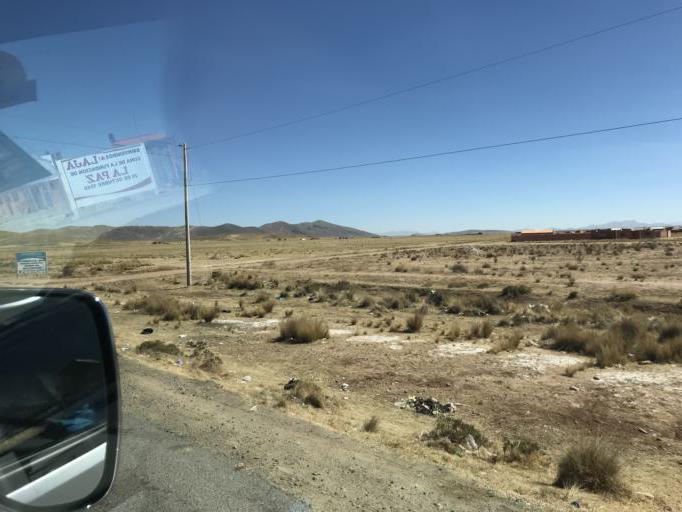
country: BO
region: La Paz
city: La Paz
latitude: -16.5312
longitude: -68.3878
